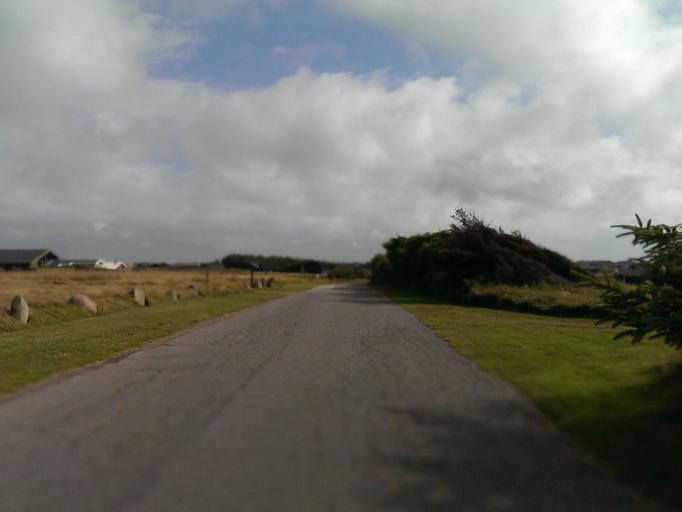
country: DK
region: North Denmark
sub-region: Jammerbugt Kommune
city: Pandrup
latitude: 57.3897
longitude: 9.7286
